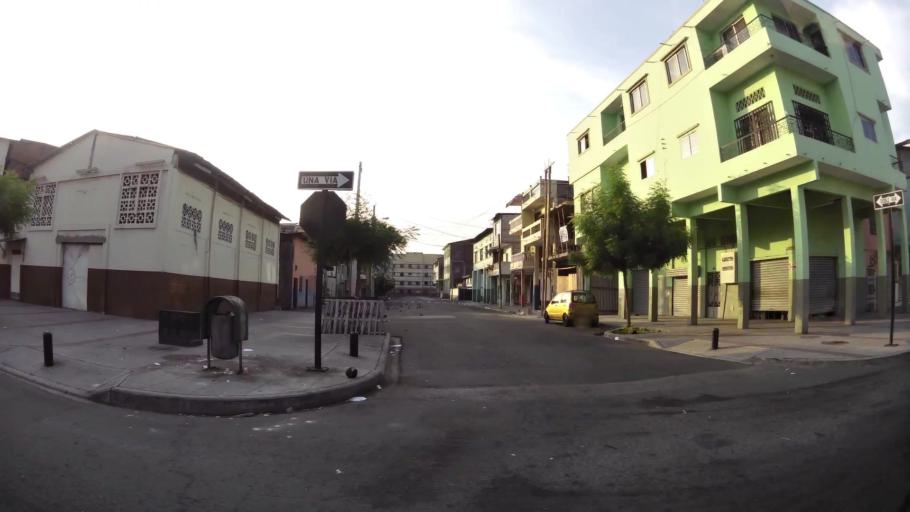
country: EC
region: Guayas
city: Guayaquil
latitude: -2.2020
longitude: -79.8984
